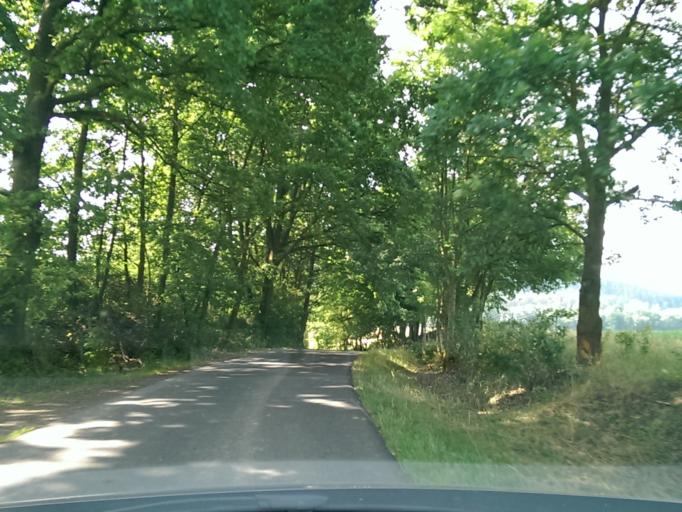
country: CZ
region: Central Bohemia
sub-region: Okres Mlada Boleslav
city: Zd'ar
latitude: 50.5397
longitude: 15.1218
